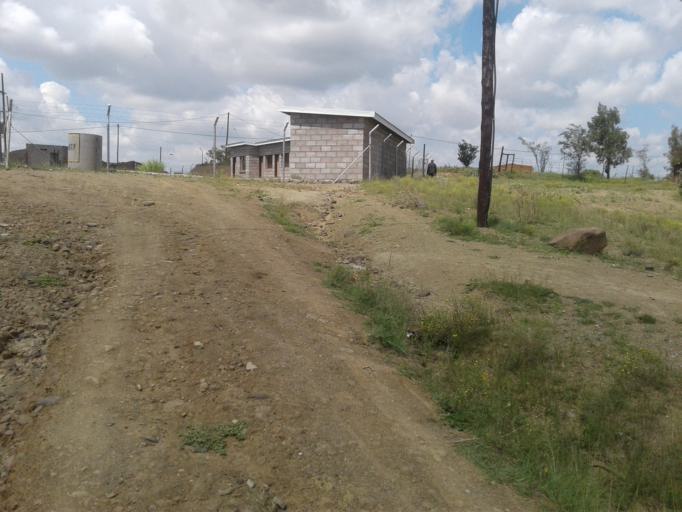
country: LS
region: Mafeteng
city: Mafeteng
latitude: -29.7542
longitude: 27.1111
